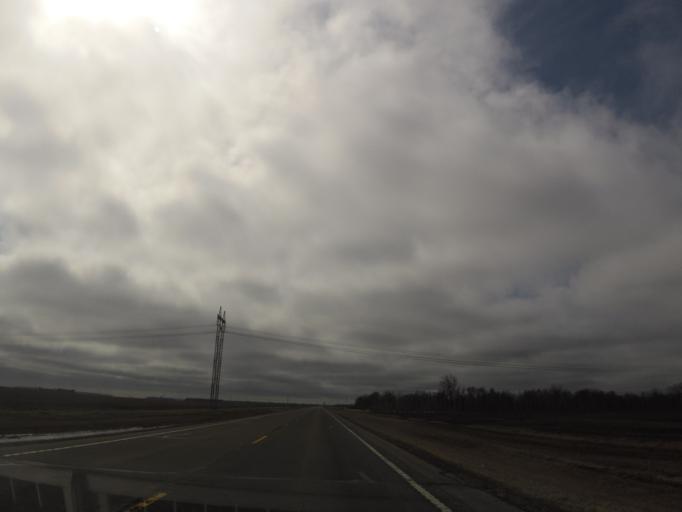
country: US
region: North Dakota
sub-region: Cass County
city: Casselton
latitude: 46.9537
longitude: -97.2197
